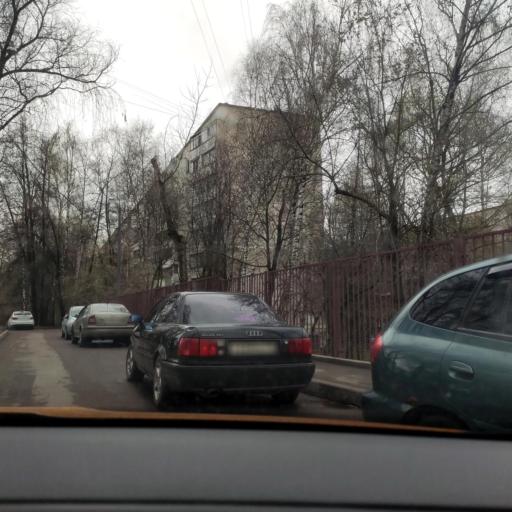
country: RU
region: Moscow
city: Nagornyy
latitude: 55.6316
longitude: 37.5991
